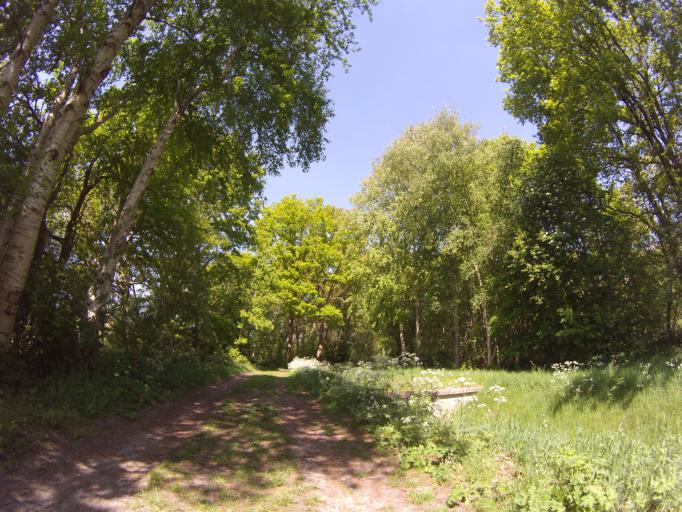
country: NL
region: Drenthe
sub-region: Gemeente Hoogeveen
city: Hoogeveen
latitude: 52.7534
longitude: 6.4970
